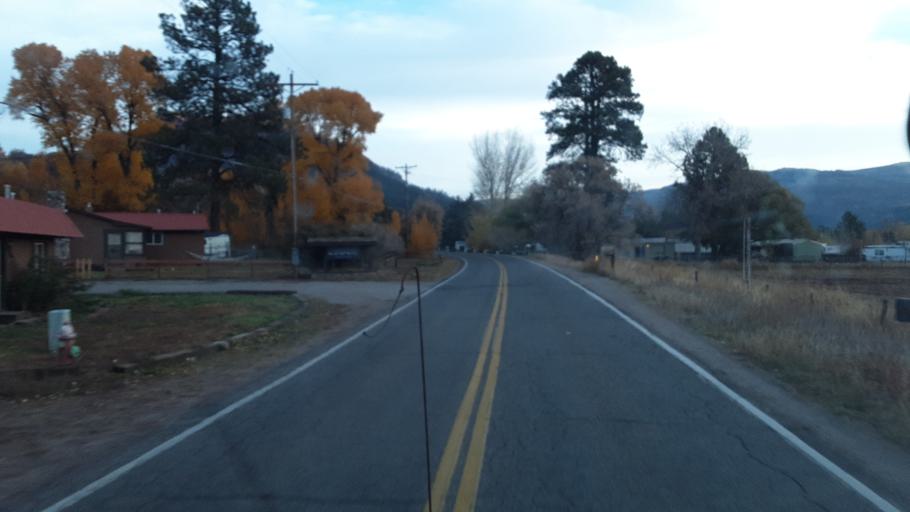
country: US
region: Colorado
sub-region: La Plata County
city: Durango
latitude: 37.4043
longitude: -107.8453
